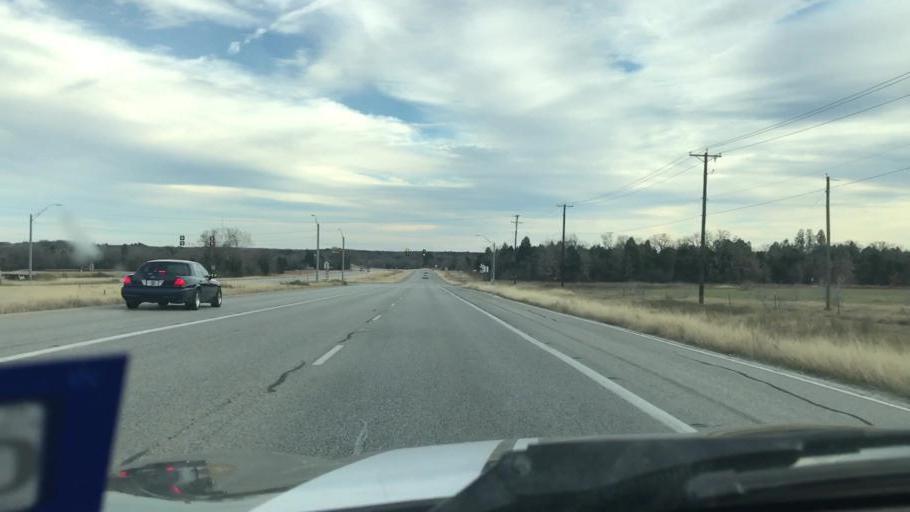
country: US
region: Texas
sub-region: Bastrop County
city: Elgin
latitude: 30.3114
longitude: -97.3064
